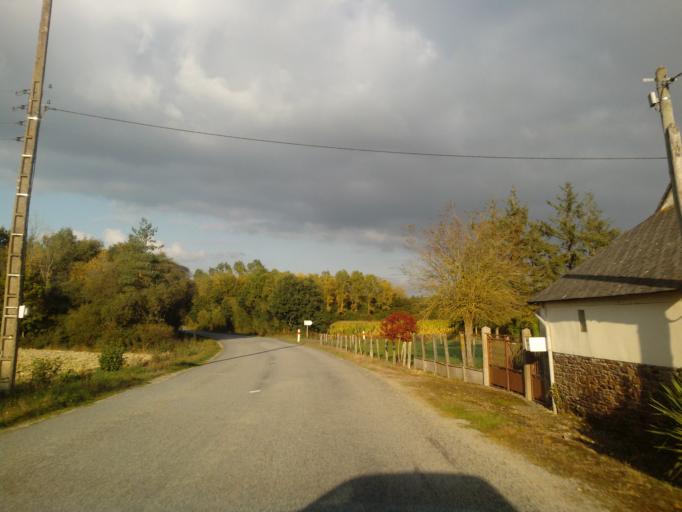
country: FR
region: Brittany
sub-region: Departement du Morbihan
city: Mauron
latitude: 48.1004
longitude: -2.3487
